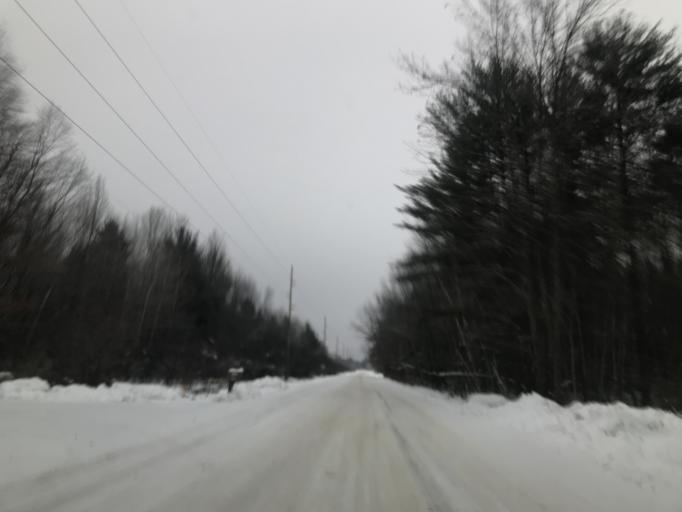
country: US
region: Wisconsin
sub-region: Marinette County
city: Peshtigo
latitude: 45.0641
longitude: -87.7361
